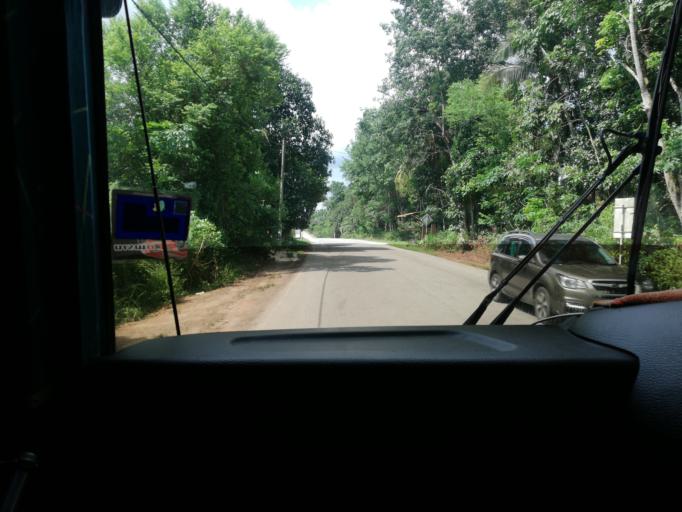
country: MY
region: Perak
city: Parit Buntar
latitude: 5.1480
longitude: 100.5916
